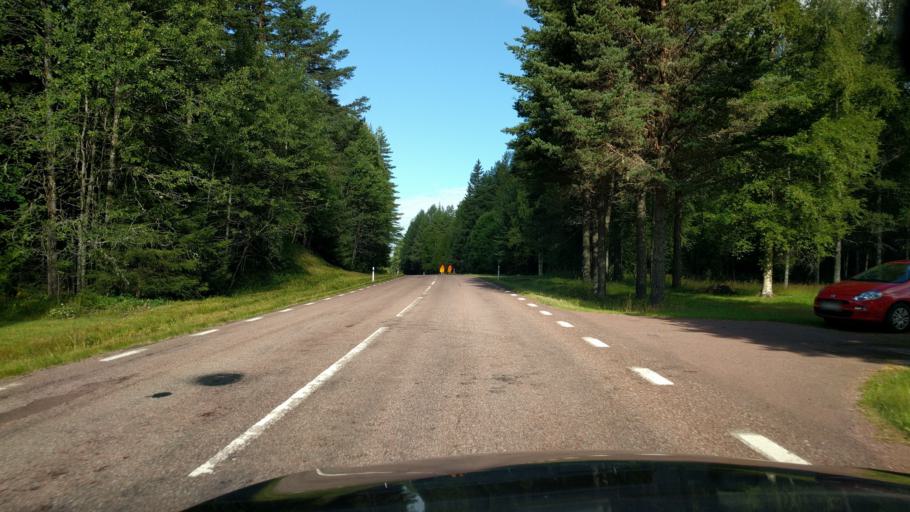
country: SE
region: Dalarna
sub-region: Mora Kommun
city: Mora
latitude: 61.0857
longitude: 14.3220
